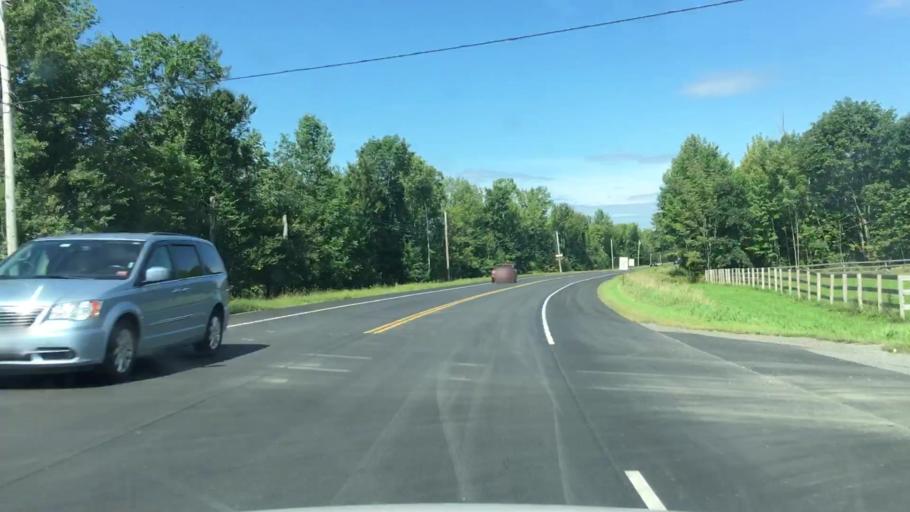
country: US
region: Maine
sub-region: Penobscot County
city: Corinna
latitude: 44.9560
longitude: -69.2625
